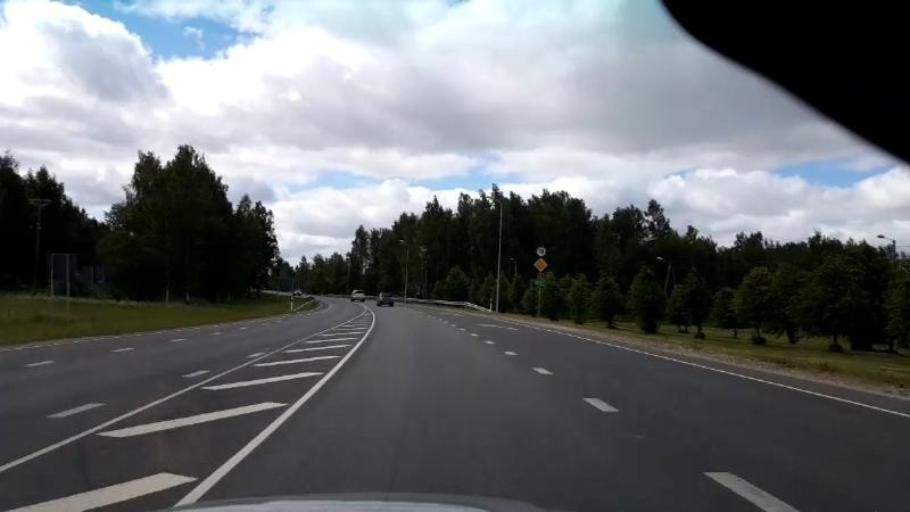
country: EE
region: Paernumaa
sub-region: Sauga vald
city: Sauga
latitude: 58.4229
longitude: 24.4947
